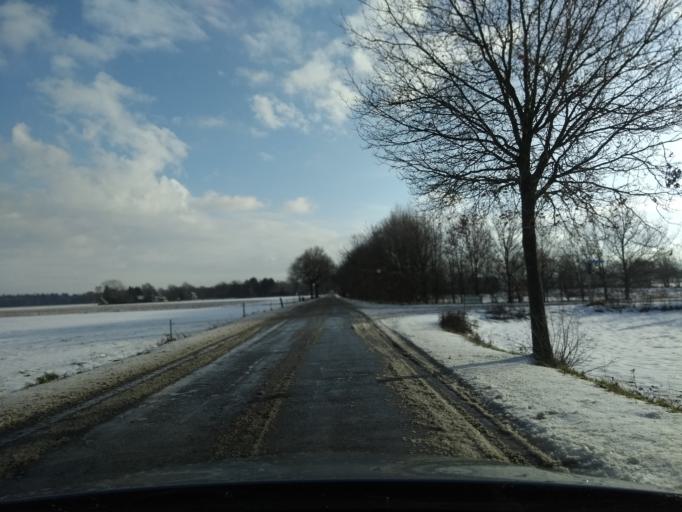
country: NL
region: Gelderland
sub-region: Gemeente Bronckhorst
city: Zelhem
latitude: 52.0338
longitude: 6.3450
